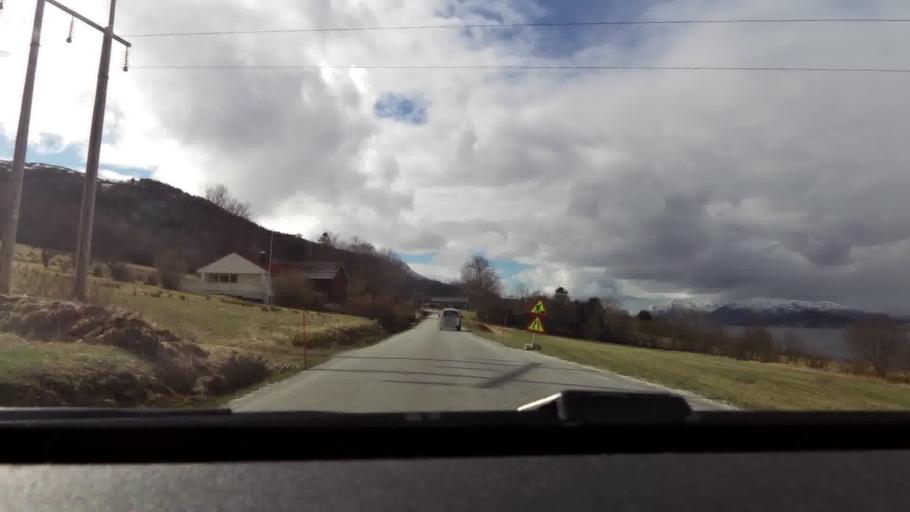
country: NO
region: More og Romsdal
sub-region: Gjemnes
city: Batnfjordsora
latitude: 62.9597
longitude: 7.6710
